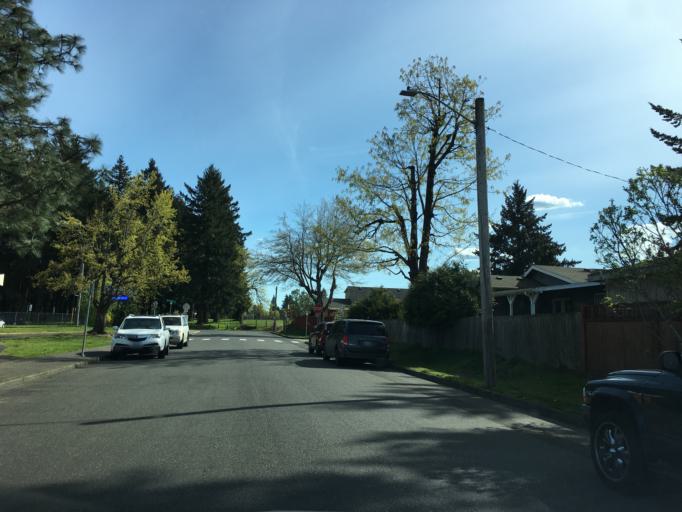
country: US
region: Oregon
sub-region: Multnomah County
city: Lents
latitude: 45.5418
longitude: -122.5323
